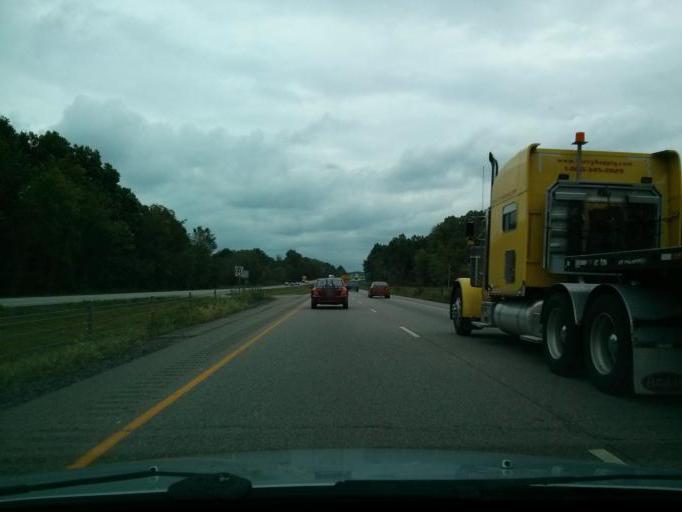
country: US
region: Ohio
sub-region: Portage County
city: Ravenna
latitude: 41.1104
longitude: -81.2559
